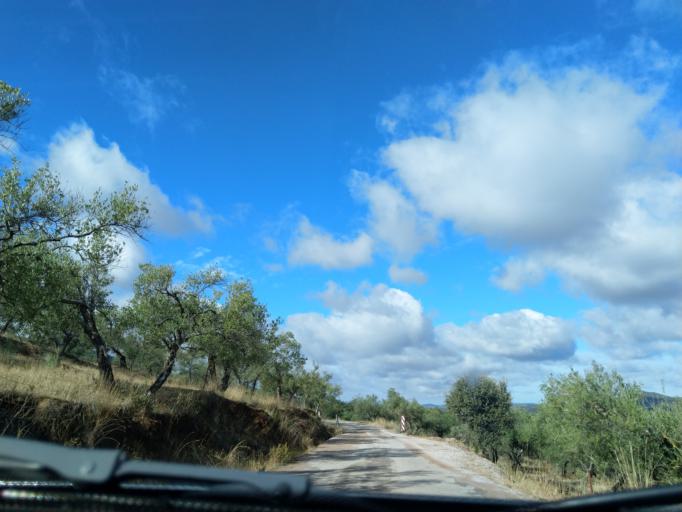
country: ES
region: Extremadura
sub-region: Provincia de Badajoz
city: Reina
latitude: 38.1291
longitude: -5.9261
